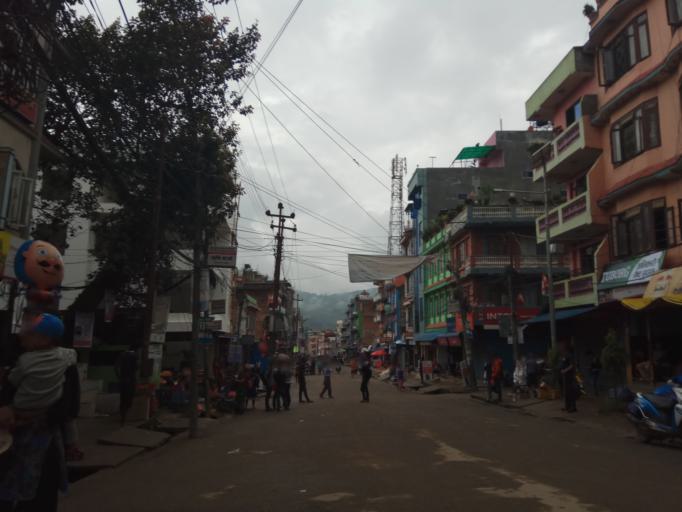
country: NP
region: Central Region
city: Kirtipur
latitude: 27.9112
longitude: 84.8929
